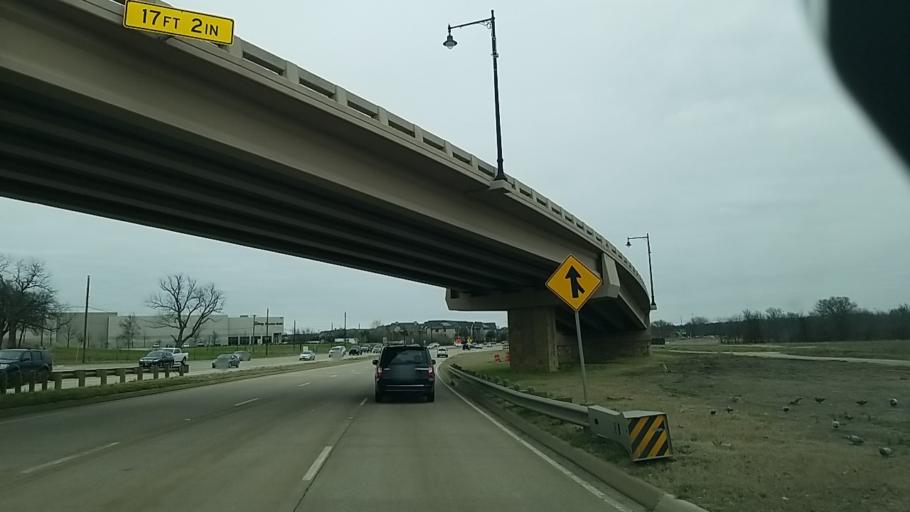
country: US
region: Texas
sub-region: Dallas County
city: Coppell
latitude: 32.9858
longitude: -97.0435
